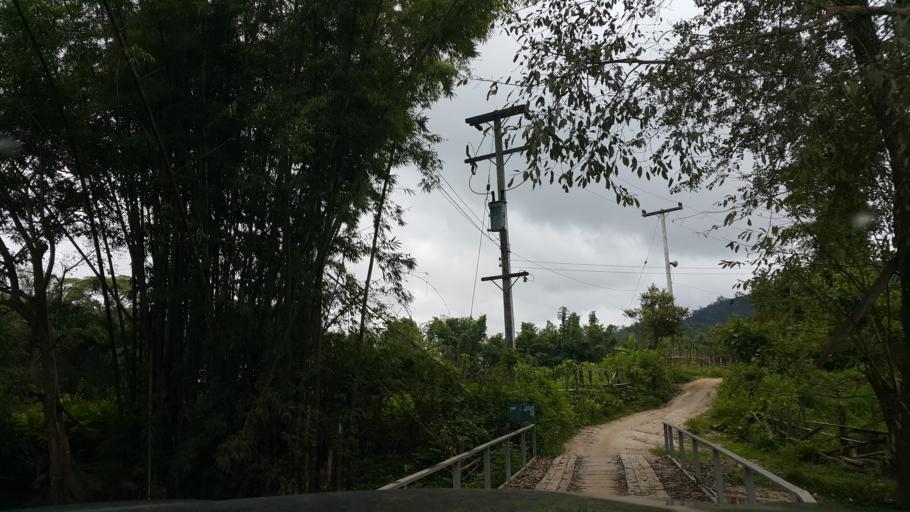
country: TH
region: Chiang Mai
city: Samoeng
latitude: 18.8103
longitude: 98.6235
